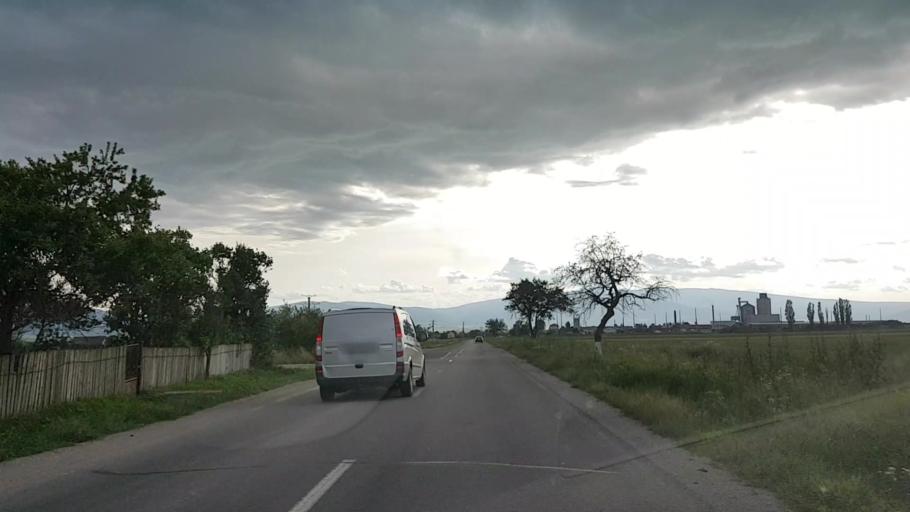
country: RO
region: Harghita
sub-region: Comuna Ciumani
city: Ciumani
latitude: 46.7094
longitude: 25.5484
